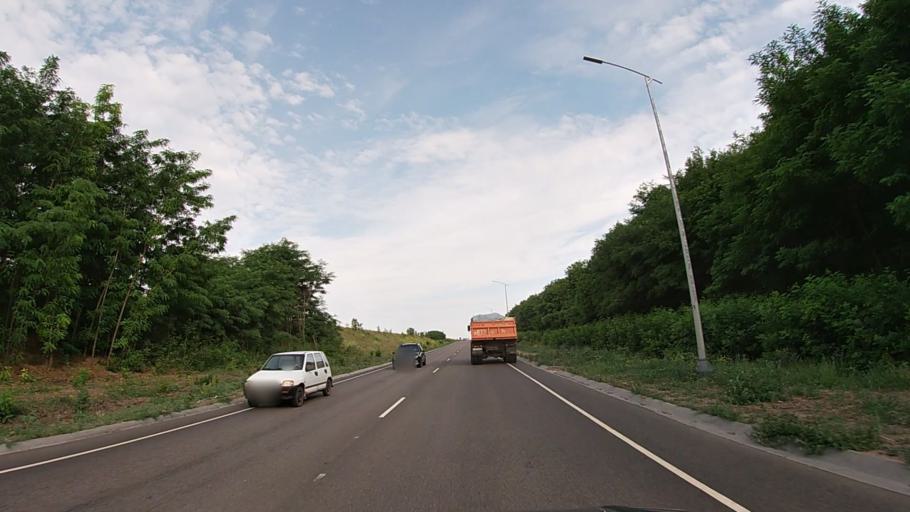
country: RU
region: Belgorod
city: Severnyy
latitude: 50.6692
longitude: 36.4881
